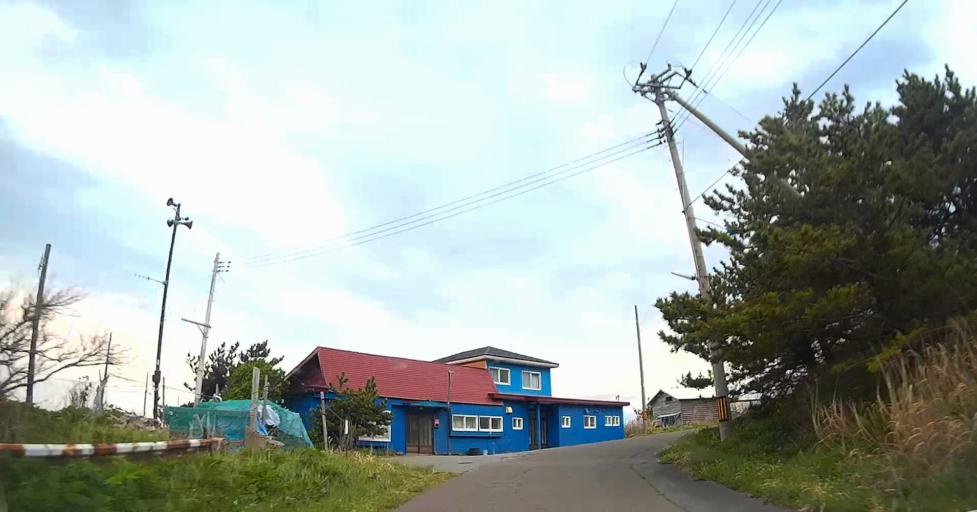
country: JP
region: Aomori
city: Shimokizukuri
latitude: 41.2430
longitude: 140.3419
